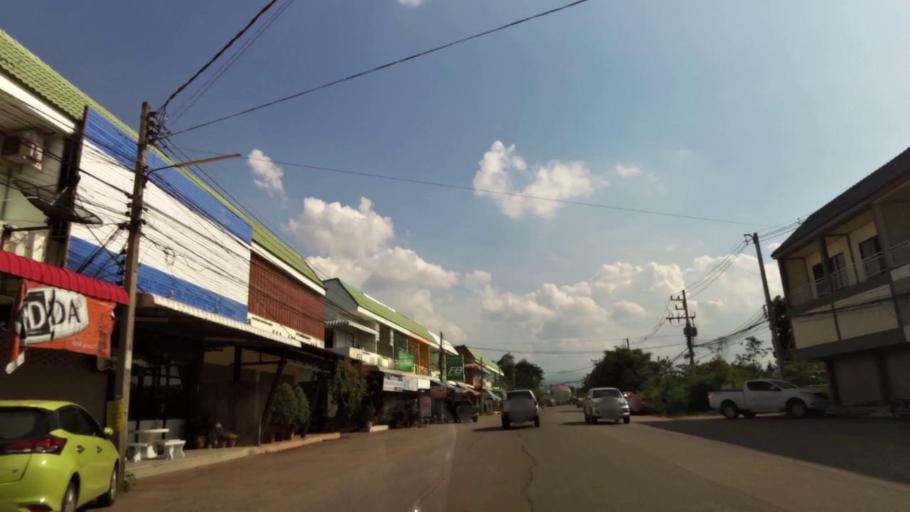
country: TH
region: Phrae
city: Phrae
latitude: 18.1249
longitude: 100.1515
